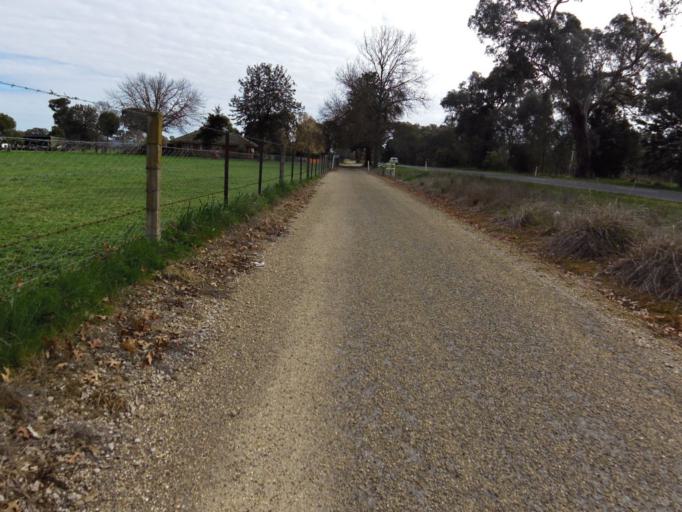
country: AU
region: Victoria
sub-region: Wangaratta
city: Wangaratta
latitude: -36.4093
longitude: 146.3511
